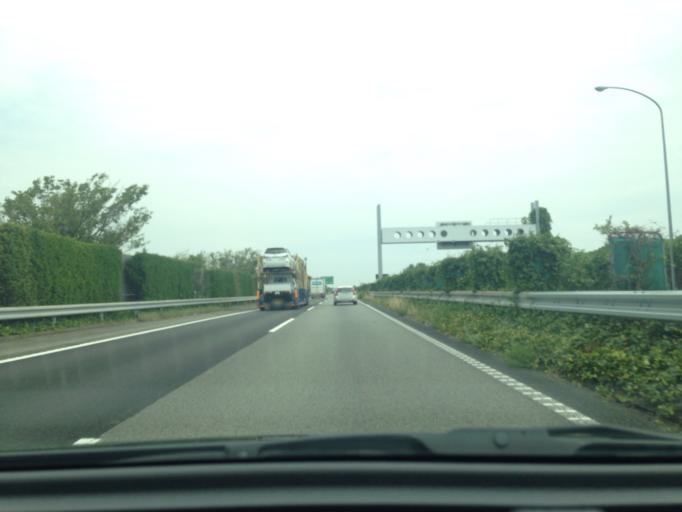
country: JP
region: Shizuoka
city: Shimada
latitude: 34.7942
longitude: 138.2372
